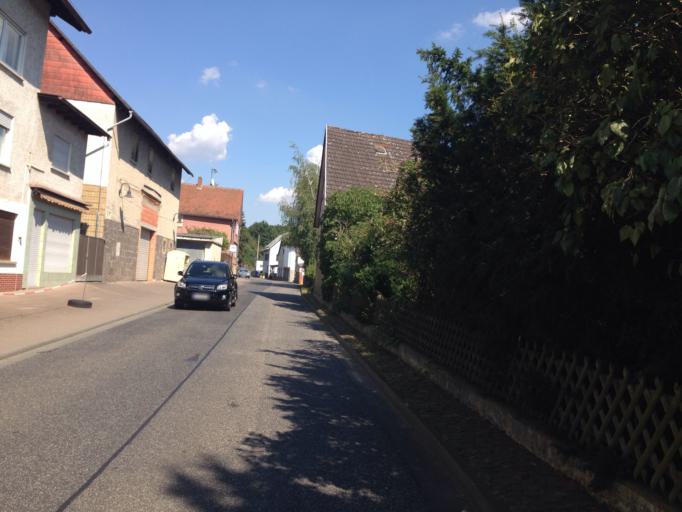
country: DE
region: Hesse
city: Beuern
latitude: 50.6684
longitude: 8.7894
